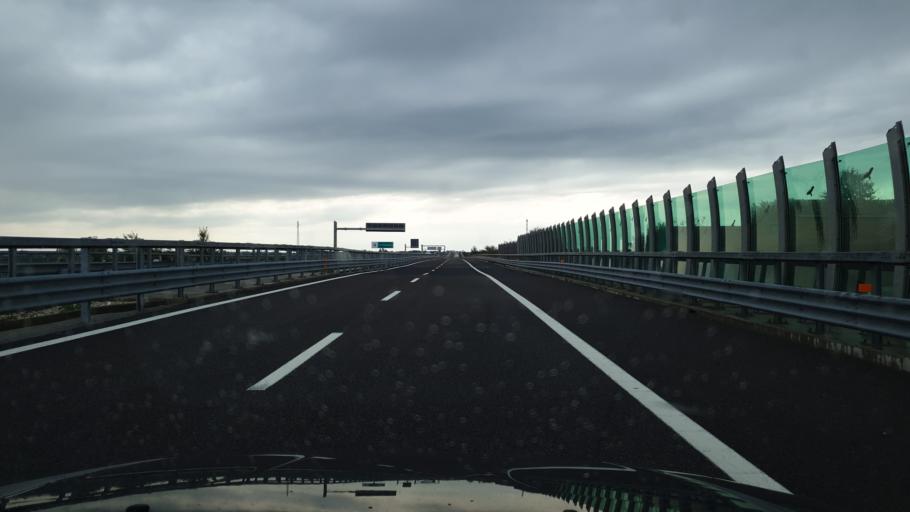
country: IT
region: Veneto
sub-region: Provincia di Rovigo
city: Badia Polesine
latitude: 45.0847
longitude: 11.5218
